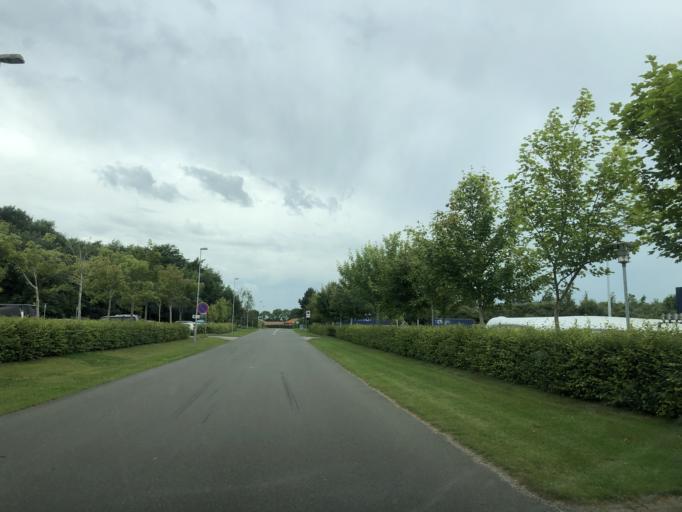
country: DK
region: Central Jutland
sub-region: Holstebro Kommune
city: Holstebro
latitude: 56.3842
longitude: 8.6048
